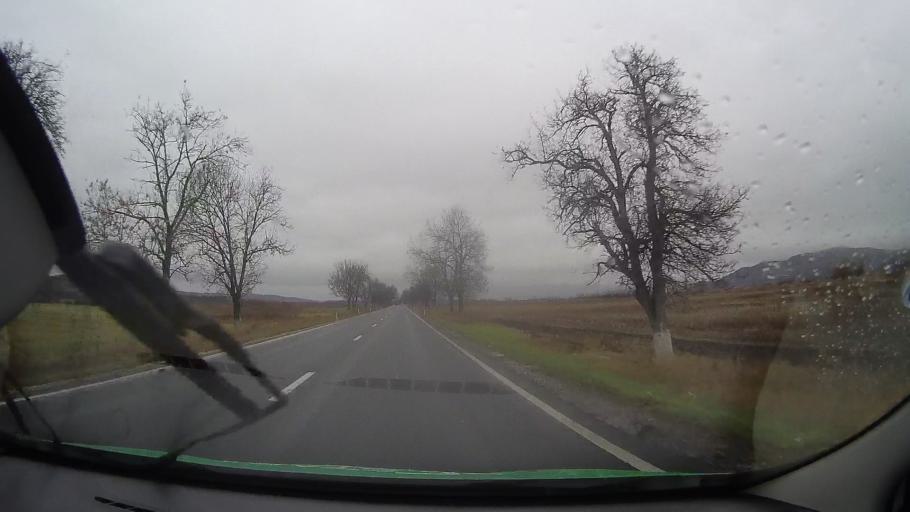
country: RO
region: Mures
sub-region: Comuna Suseni
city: Suseni
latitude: 46.8265
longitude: 24.7392
